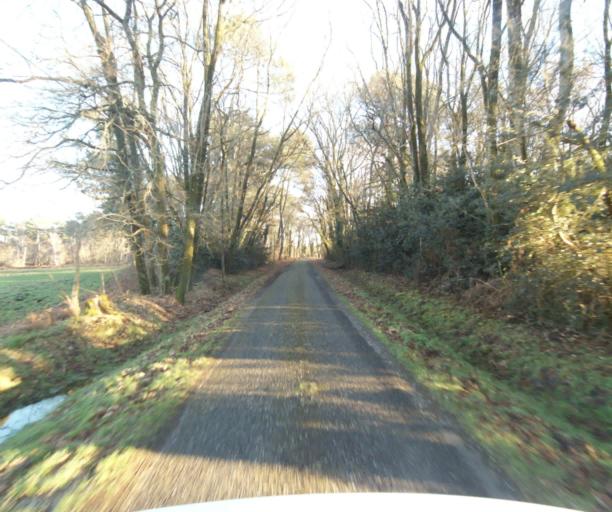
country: FR
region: Aquitaine
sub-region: Departement des Landes
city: Gabarret
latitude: 44.1090
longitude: -0.0801
